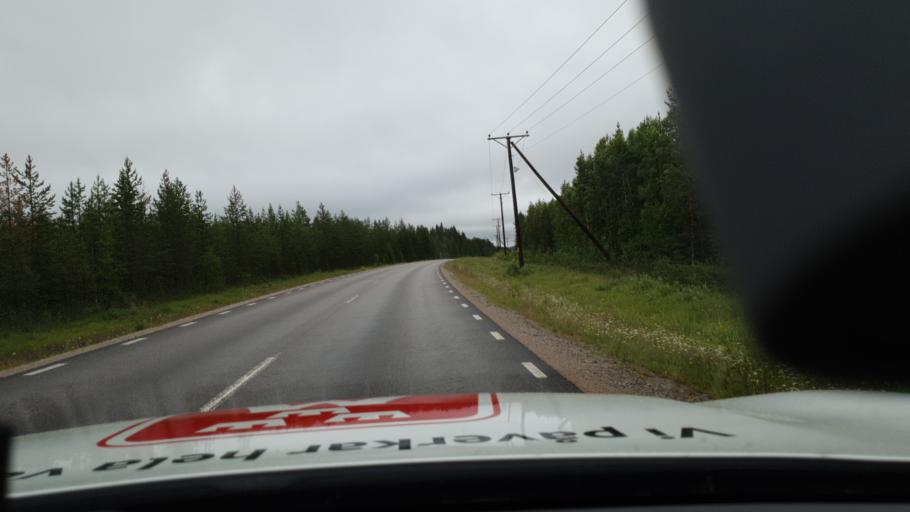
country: SE
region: Norrbotten
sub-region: Overtornea Kommun
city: OEvertornea
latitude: 66.3988
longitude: 23.5703
